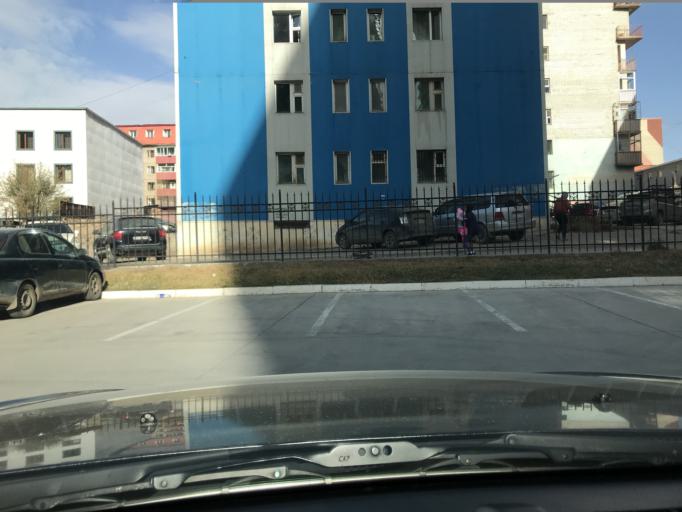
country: MN
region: Ulaanbaatar
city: Ulaanbaatar
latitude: 47.9197
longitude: 106.9442
